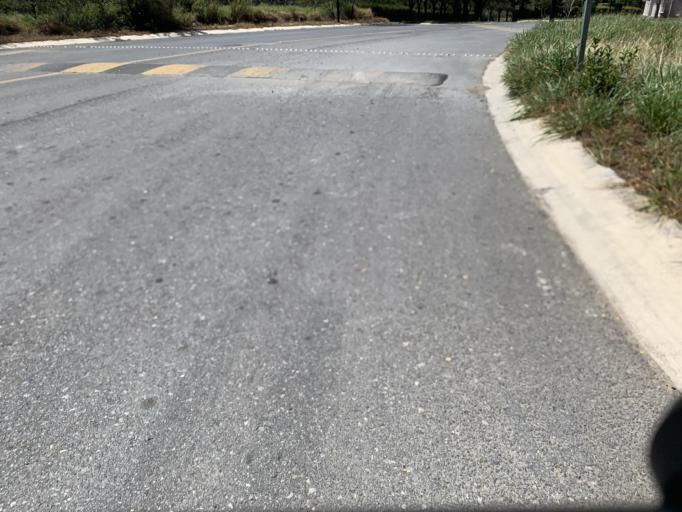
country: MX
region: Nuevo Leon
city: Santiago
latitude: 25.5073
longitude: -100.1836
